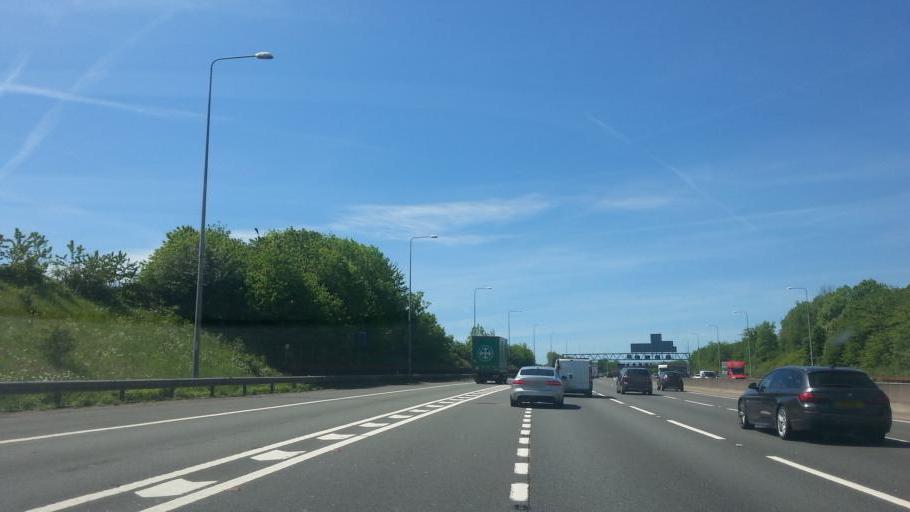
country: GB
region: England
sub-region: Hertfordshire
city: Abbots Langley
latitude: 51.7148
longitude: -0.3923
